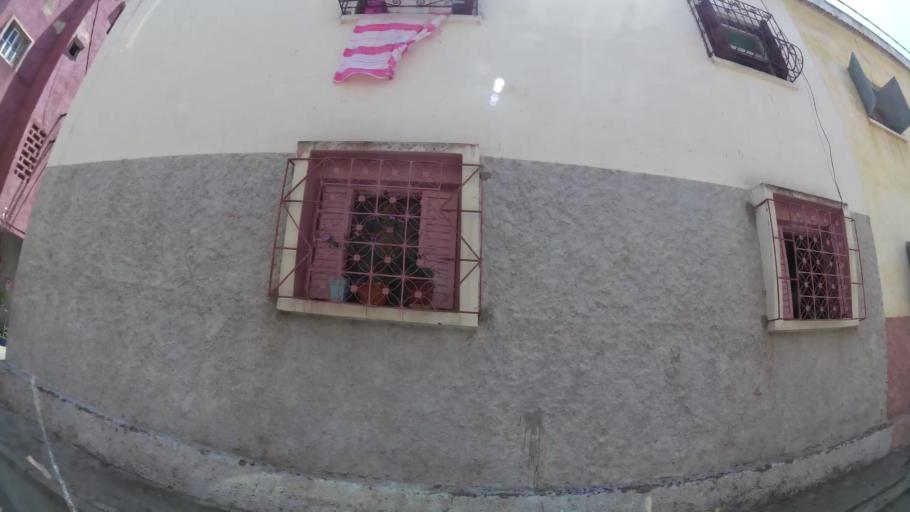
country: MA
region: Gharb-Chrarda-Beni Hssen
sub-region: Kenitra Province
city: Kenitra
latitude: 34.2657
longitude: -6.5547
